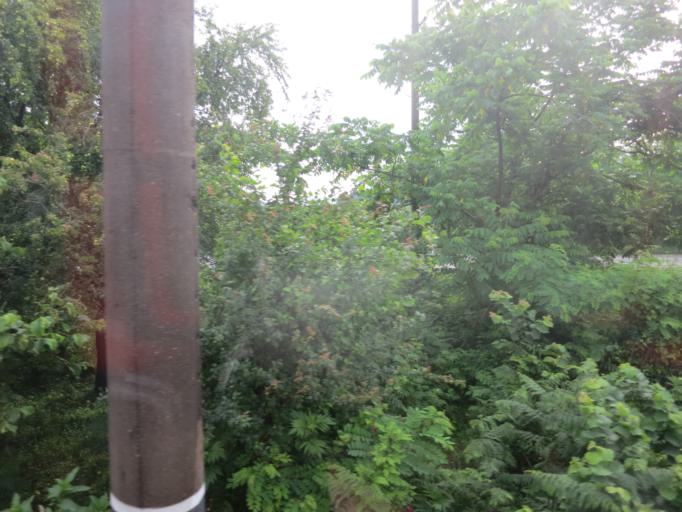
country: GE
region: Guria
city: Urek'i
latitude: 41.9874
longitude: 41.7823
